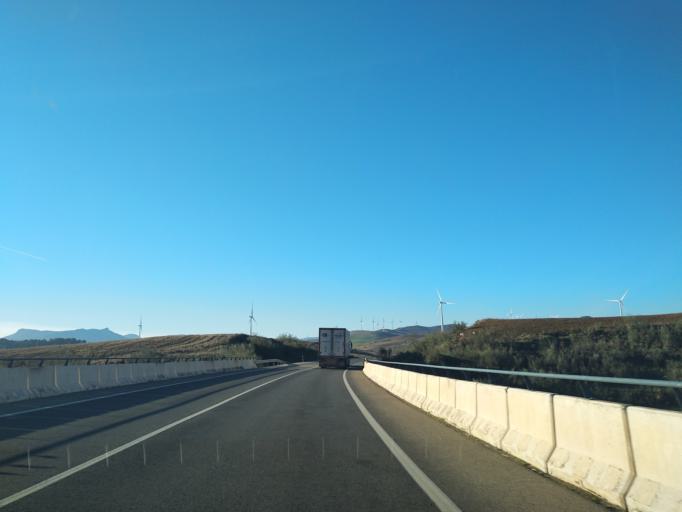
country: ES
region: Andalusia
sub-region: Provincia de Malaga
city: Teba
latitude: 36.9551
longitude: -4.8589
